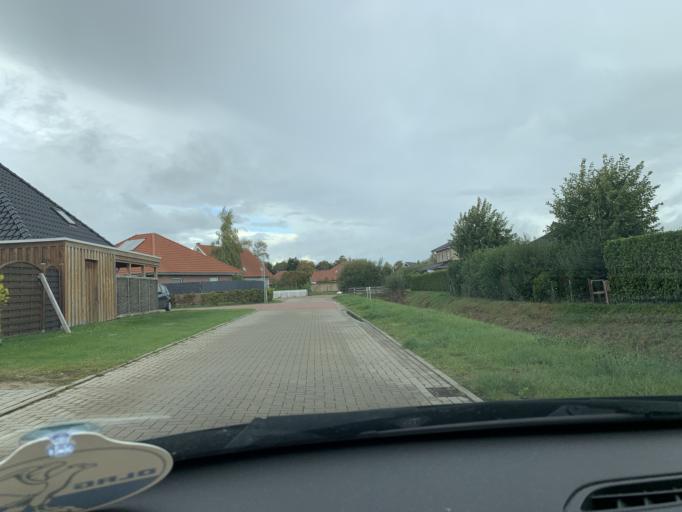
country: DE
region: Lower Saxony
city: Apen
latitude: 53.2270
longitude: 7.7704
